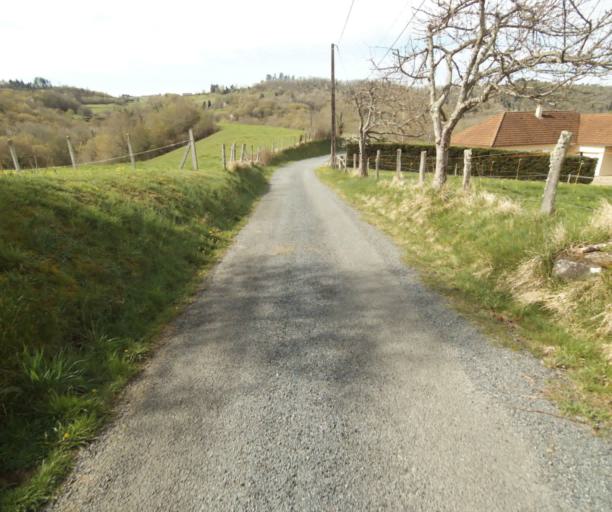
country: FR
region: Limousin
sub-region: Departement de la Correze
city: Laguenne
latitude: 45.2452
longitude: 1.8115
